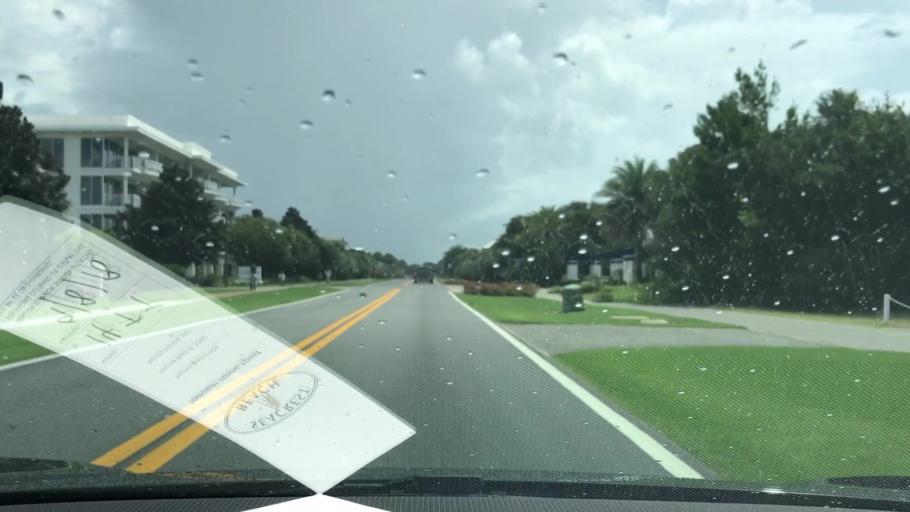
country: US
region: Florida
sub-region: Bay County
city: Laguna Beach
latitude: 30.2833
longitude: -86.0251
